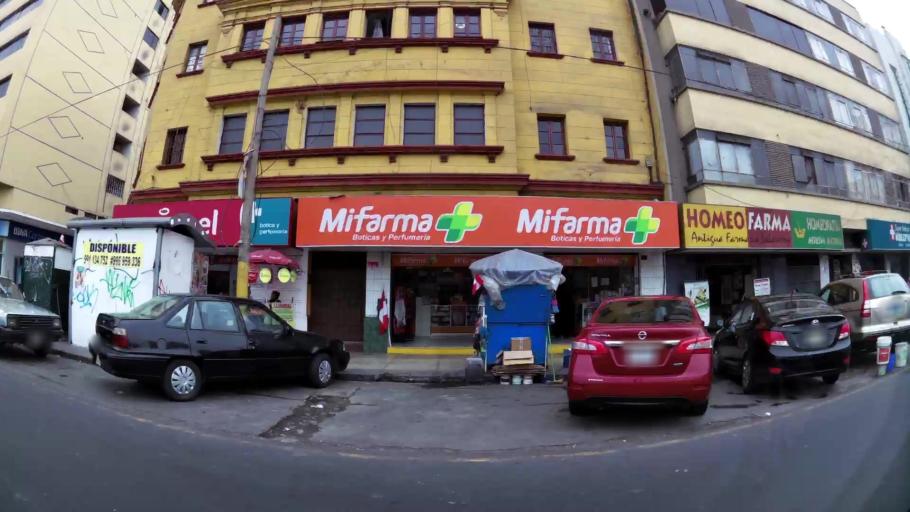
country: PE
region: Lima
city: Lima
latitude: -12.0546
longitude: -77.0432
